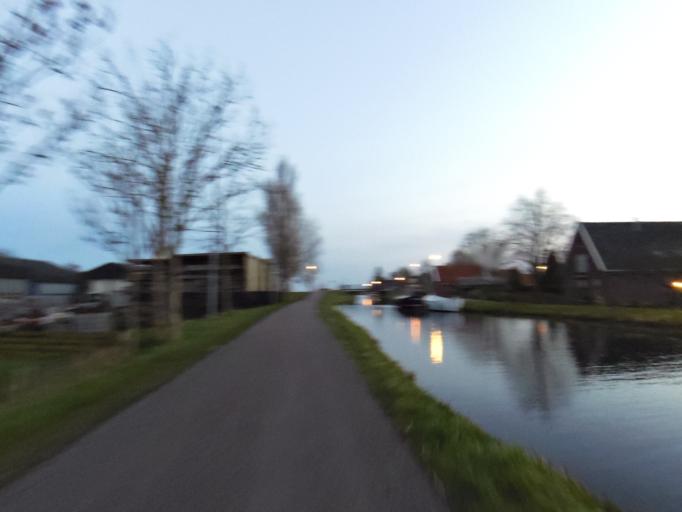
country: NL
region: South Holland
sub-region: Gemeente Leiderdorp
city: Leiderdorp
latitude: 52.1660
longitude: 4.5639
